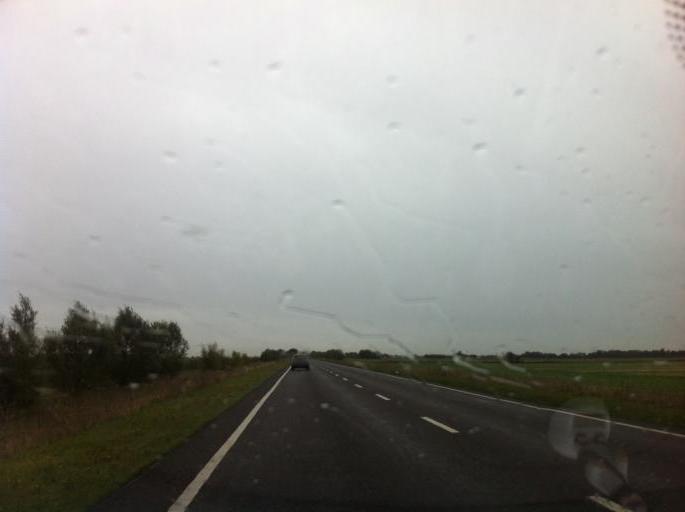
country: GB
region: England
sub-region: Peterborough
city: Eye
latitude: 52.6227
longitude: -0.2055
